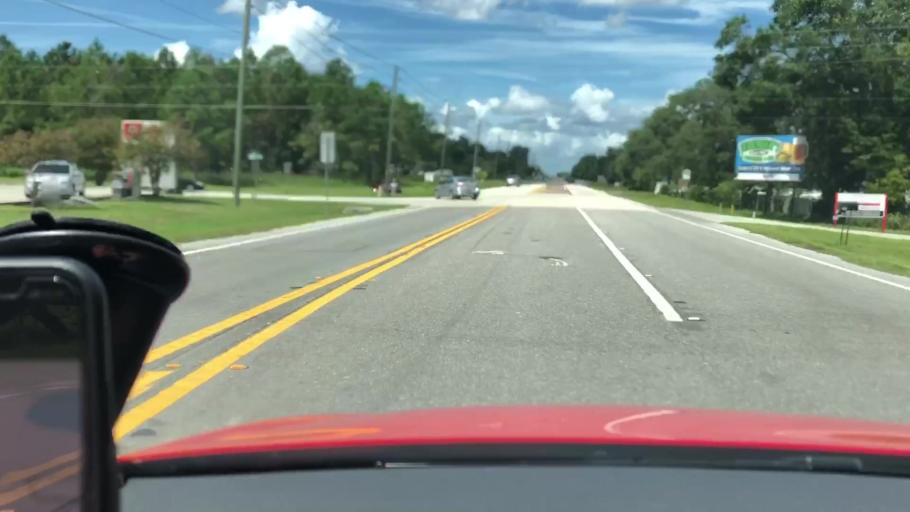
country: US
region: Florida
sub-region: Lake County
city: Eustis
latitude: 28.8530
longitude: -81.6540
